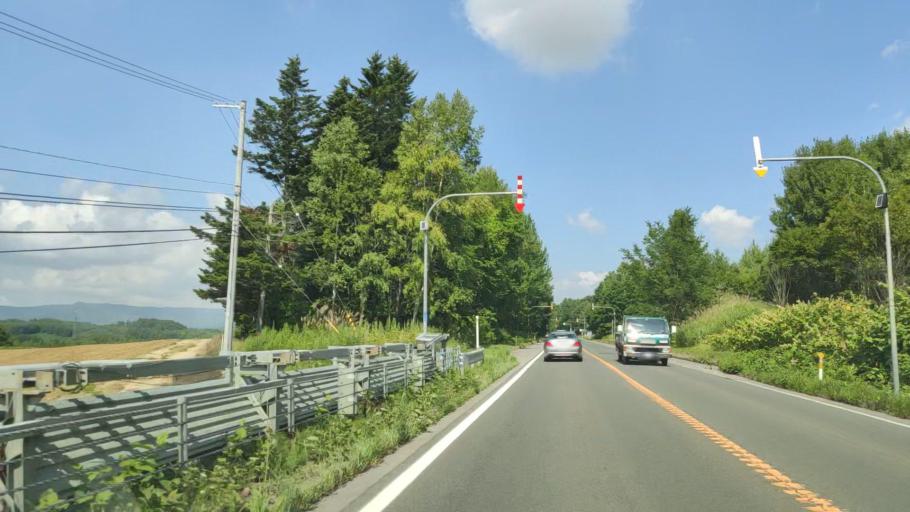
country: JP
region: Hokkaido
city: Shimo-furano
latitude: 43.5084
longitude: 142.4556
